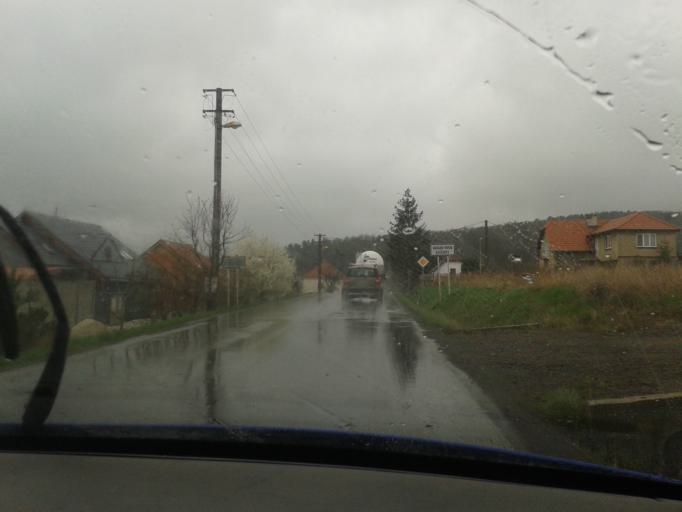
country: CZ
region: Central Bohemia
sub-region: Okres Beroun
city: Kraluv Dvur
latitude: 49.9286
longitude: 14.0388
